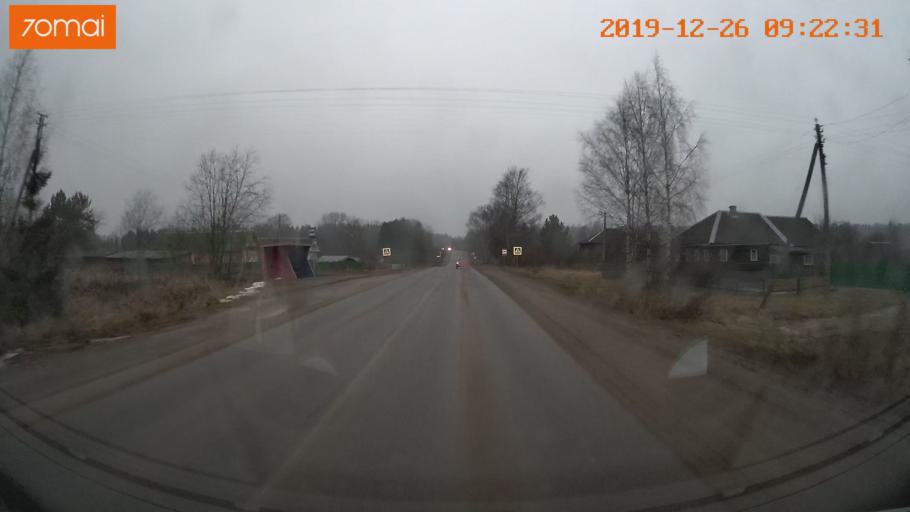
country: RU
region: Vologda
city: Gryazovets
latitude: 58.9816
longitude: 40.2151
